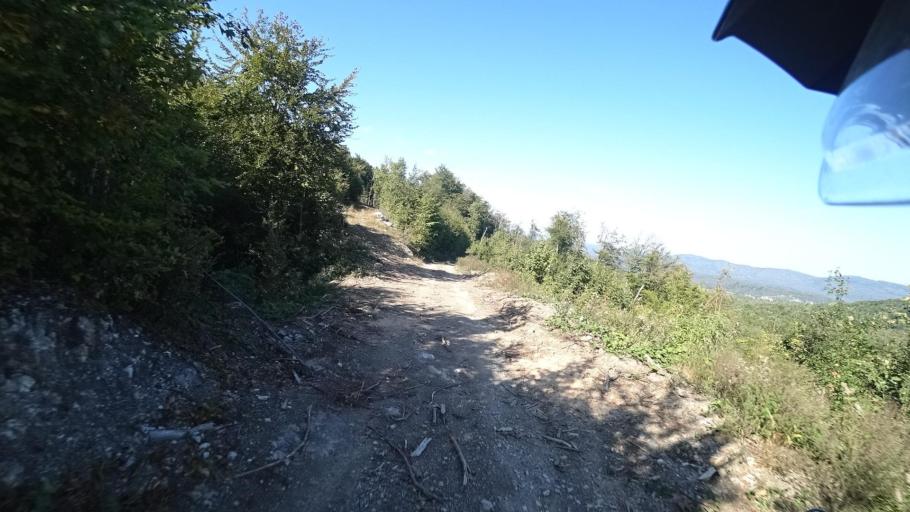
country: HR
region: Primorsko-Goranska
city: Vrbovsko
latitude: 45.2966
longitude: 15.1323
